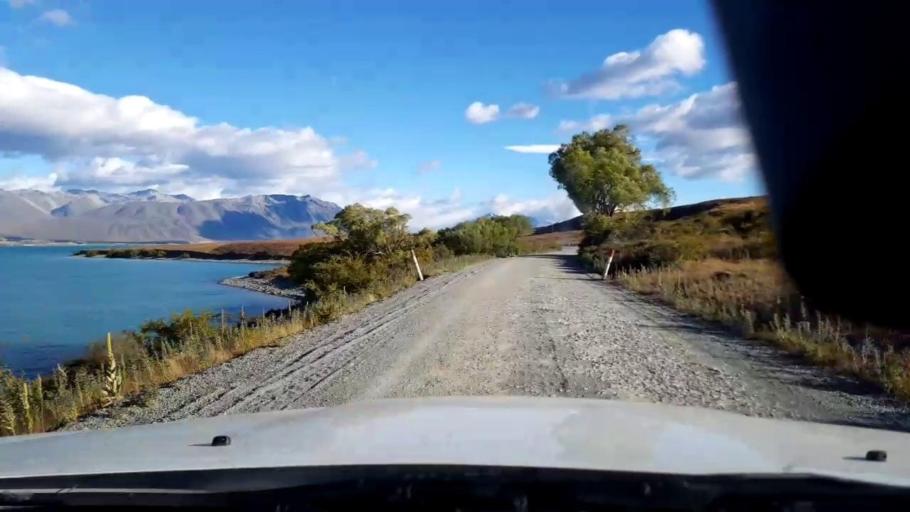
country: NZ
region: Canterbury
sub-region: Timaru District
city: Pleasant Point
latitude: -43.9278
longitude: 170.5604
